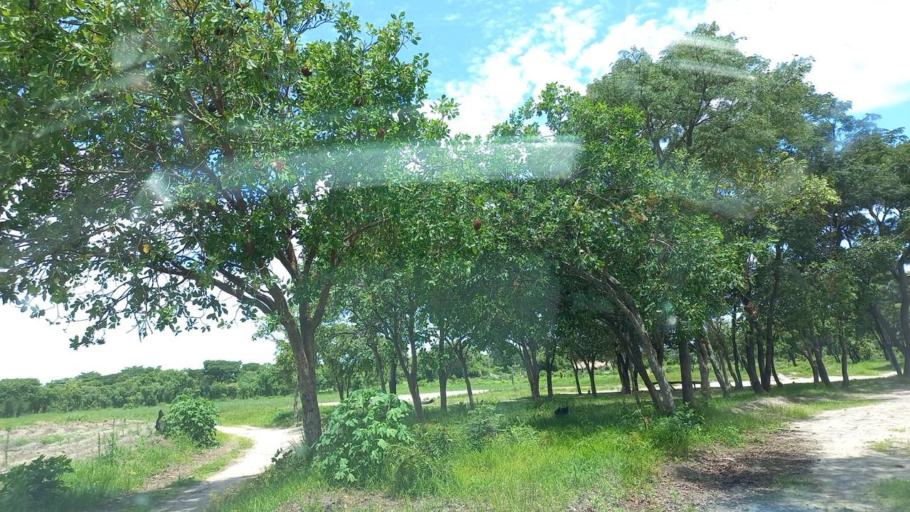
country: ZM
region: Copperbelt
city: Ndola
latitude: -12.8685
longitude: 28.4435
